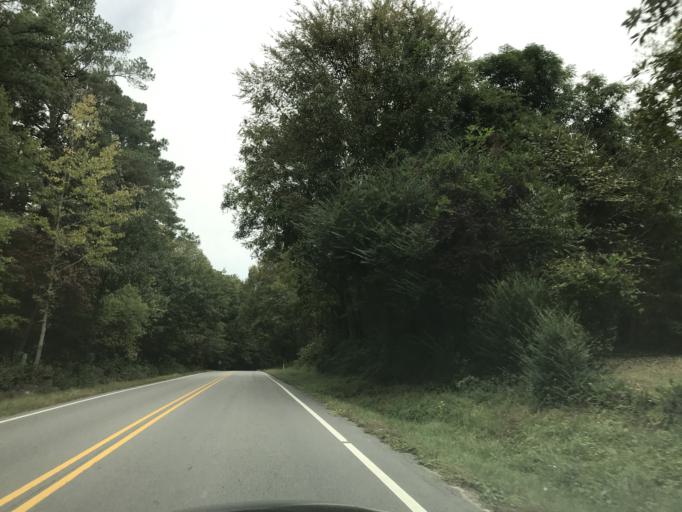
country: US
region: North Carolina
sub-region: Wake County
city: Knightdale
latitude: 35.8159
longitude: -78.5005
